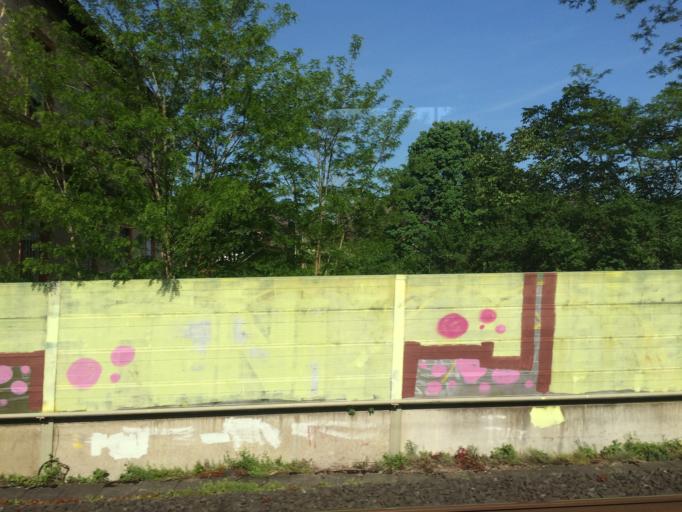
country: DE
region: North Rhine-Westphalia
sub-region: Regierungsbezirk Dusseldorf
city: Langenfeld
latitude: 51.0986
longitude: 6.9409
